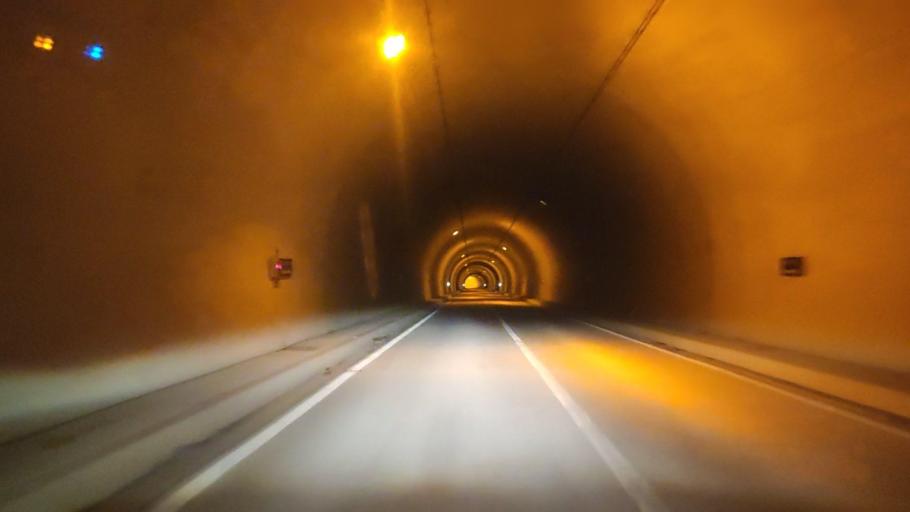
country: JP
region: Kumamoto
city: Matsubase
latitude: 32.5061
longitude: 130.9188
